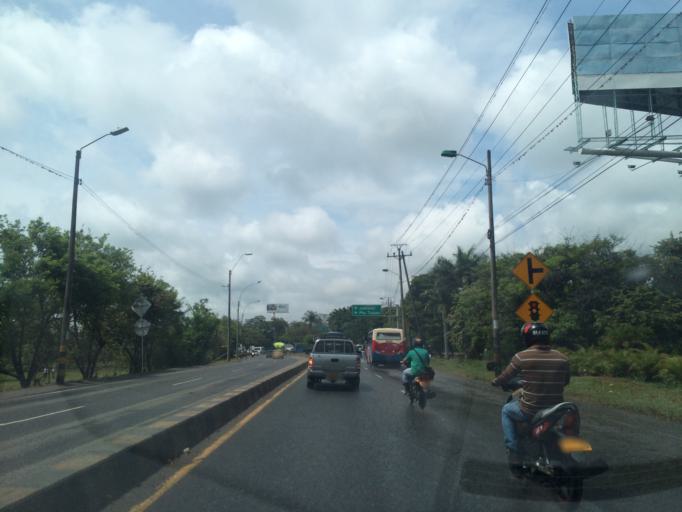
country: CO
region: Valle del Cauca
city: Jamundi
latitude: 3.3460
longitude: -76.5242
